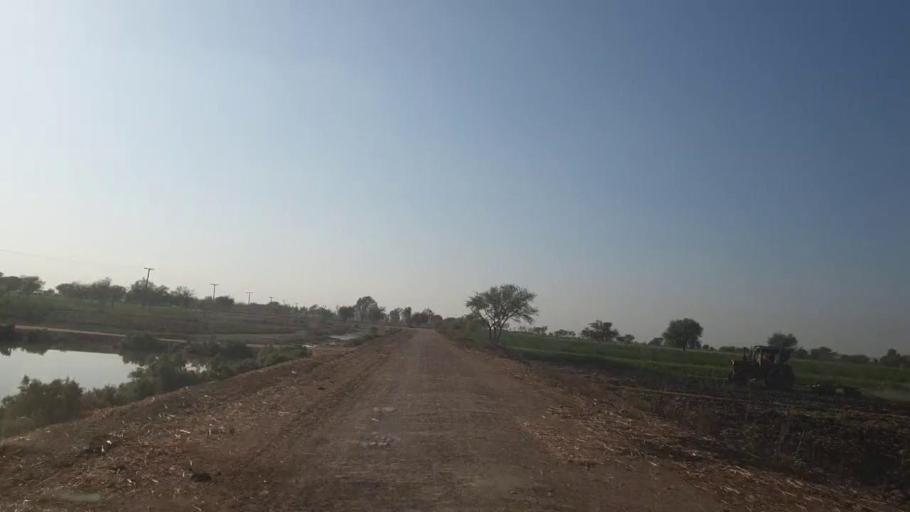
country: PK
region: Sindh
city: Mirwah Gorchani
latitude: 25.4303
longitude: 69.1248
